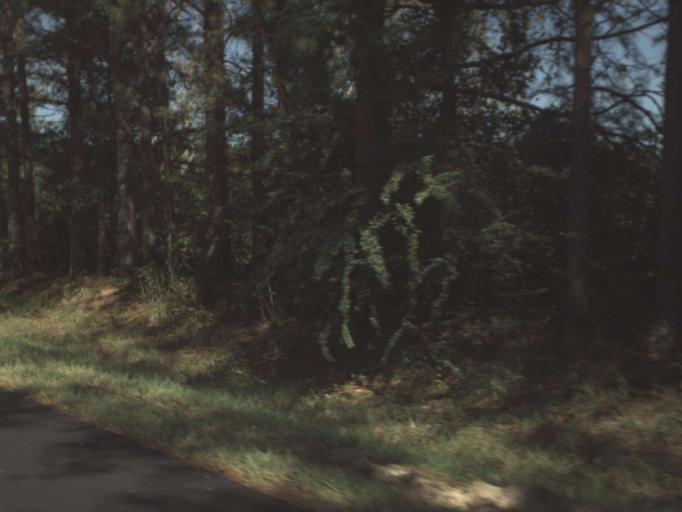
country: US
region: Alabama
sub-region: Covington County
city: Florala
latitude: 30.8619
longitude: -86.2513
